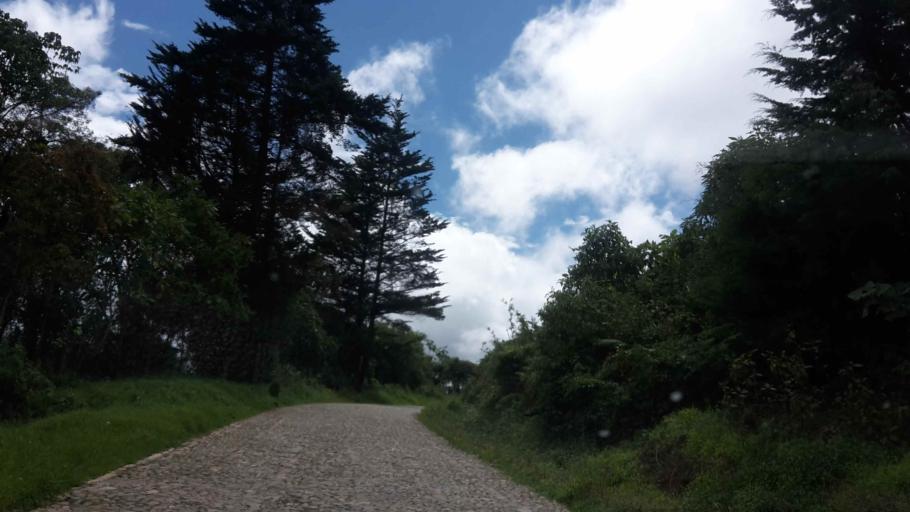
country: BO
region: Cochabamba
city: Colomi
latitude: -17.1431
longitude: -65.9178
